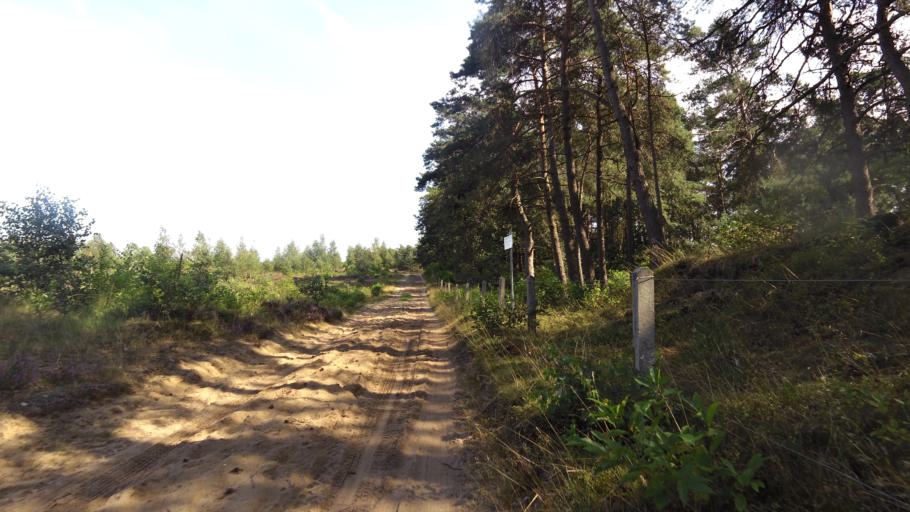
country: NL
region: Gelderland
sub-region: Gemeente Ede
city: Otterlo
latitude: 52.1513
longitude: 5.8472
